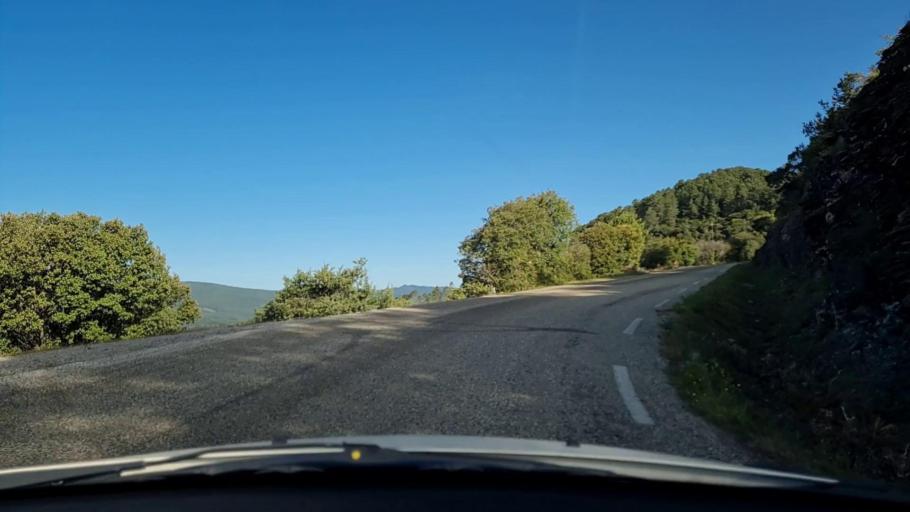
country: FR
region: Languedoc-Roussillon
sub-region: Departement du Gard
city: Branoux-les-Taillades
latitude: 44.1838
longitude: 3.9892
